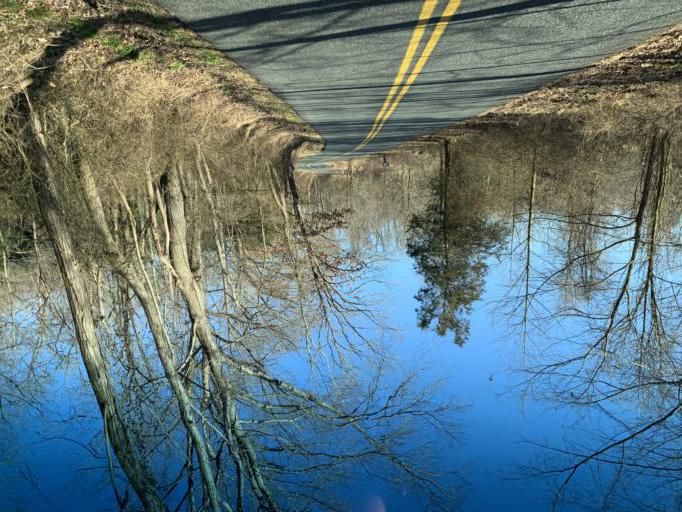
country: US
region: Maryland
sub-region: Harford County
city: South Bel Air
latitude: 39.6208
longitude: -76.2536
